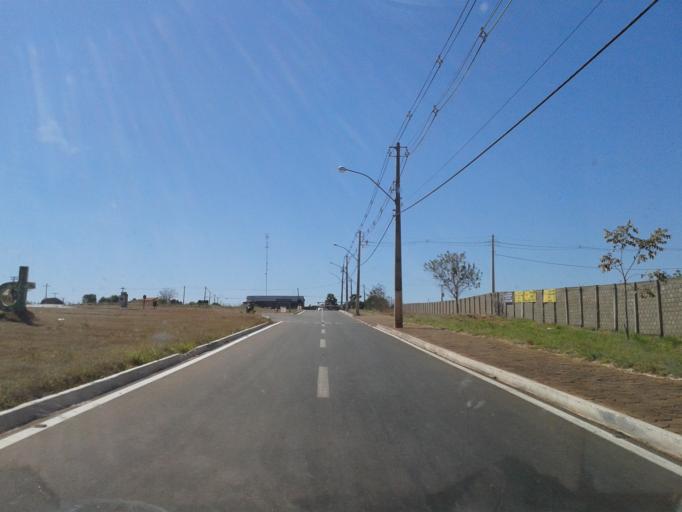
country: BR
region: Goias
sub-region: Sao Miguel Do Araguaia
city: Sao Miguel do Araguaia
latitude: -13.2683
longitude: -50.1563
